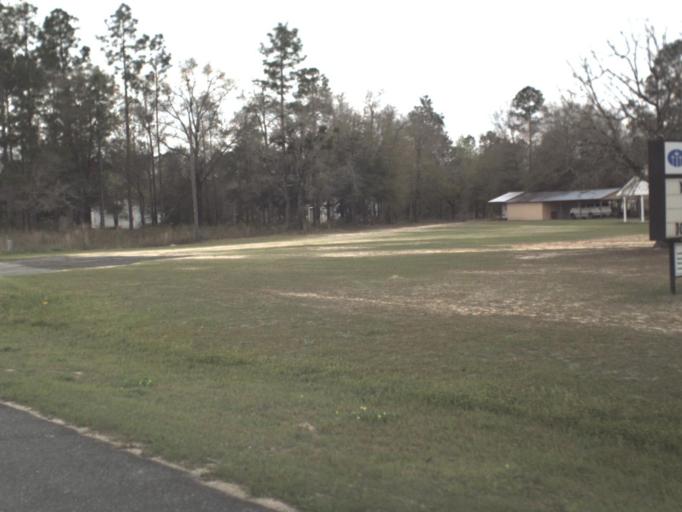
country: US
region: Florida
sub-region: Calhoun County
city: Blountstown
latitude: 30.4515
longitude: -85.1841
